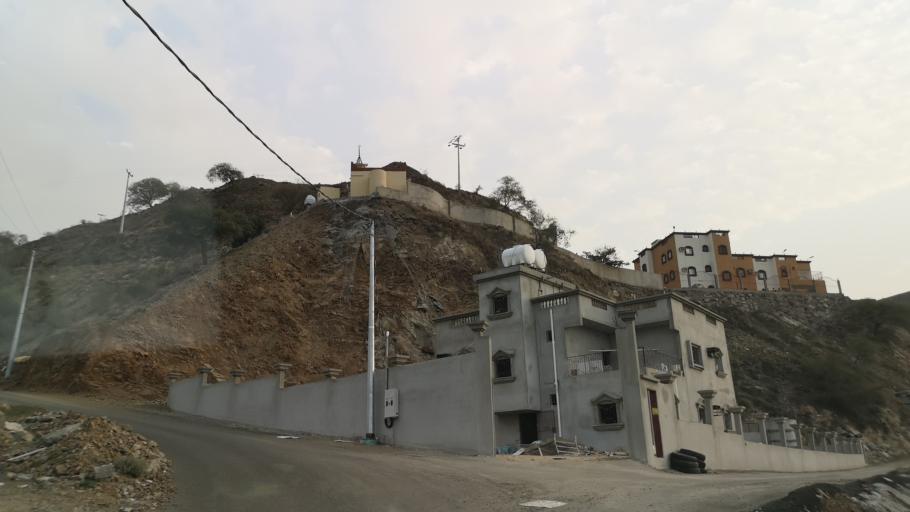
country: YE
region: Sa'dah
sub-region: Monabbih
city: Suq al Khamis
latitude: 17.3279
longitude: 43.1449
